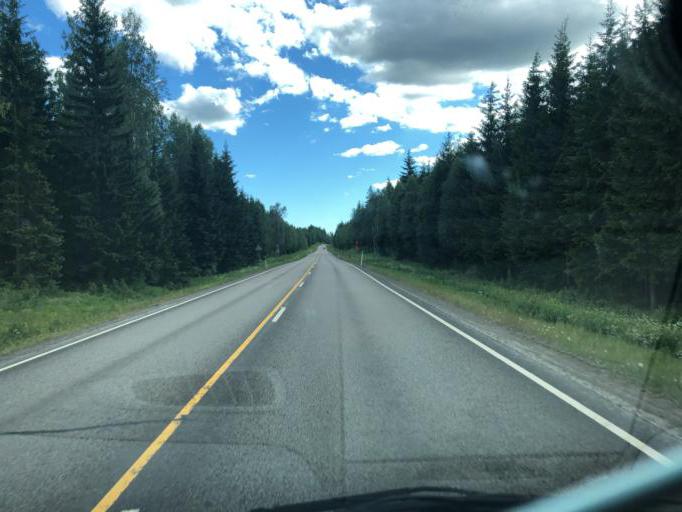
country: FI
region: Kymenlaakso
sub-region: Kouvola
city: Kouvola
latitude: 61.0150
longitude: 26.9524
